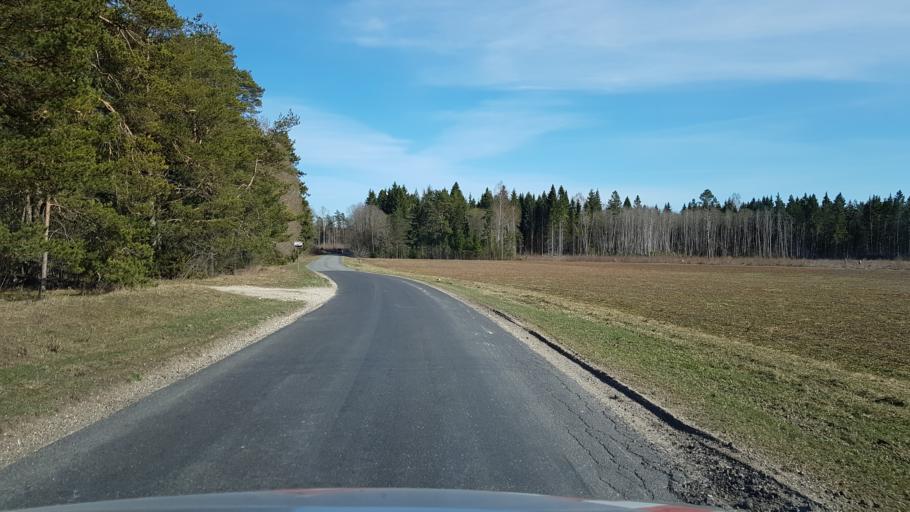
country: EE
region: Harju
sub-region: Nissi vald
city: Riisipere
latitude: 59.0992
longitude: 24.3249
